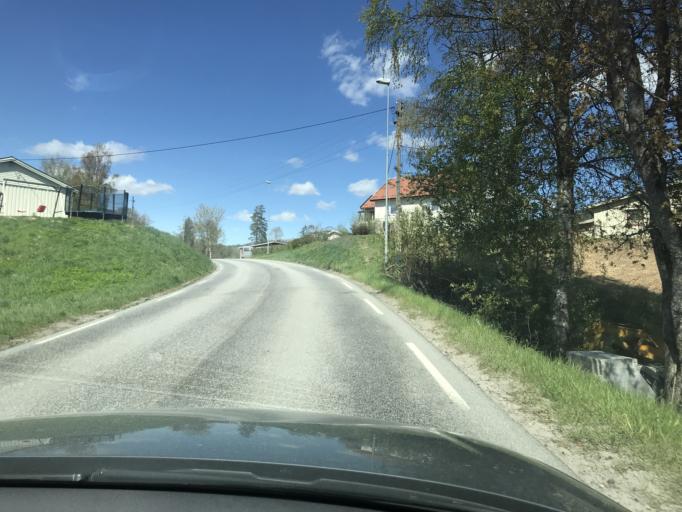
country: NO
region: Telemark
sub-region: Hjartdal
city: Sauland
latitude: 59.6168
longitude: 8.9486
